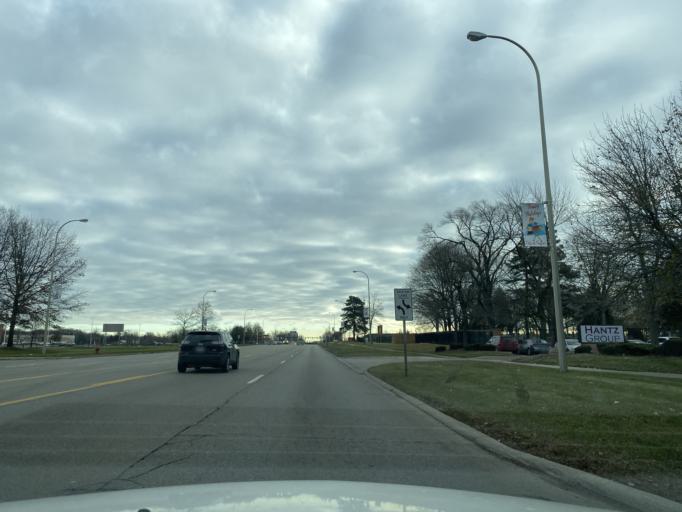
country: US
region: Michigan
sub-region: Wayne County
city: Taylor
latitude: 42.1978
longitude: -83.2565
